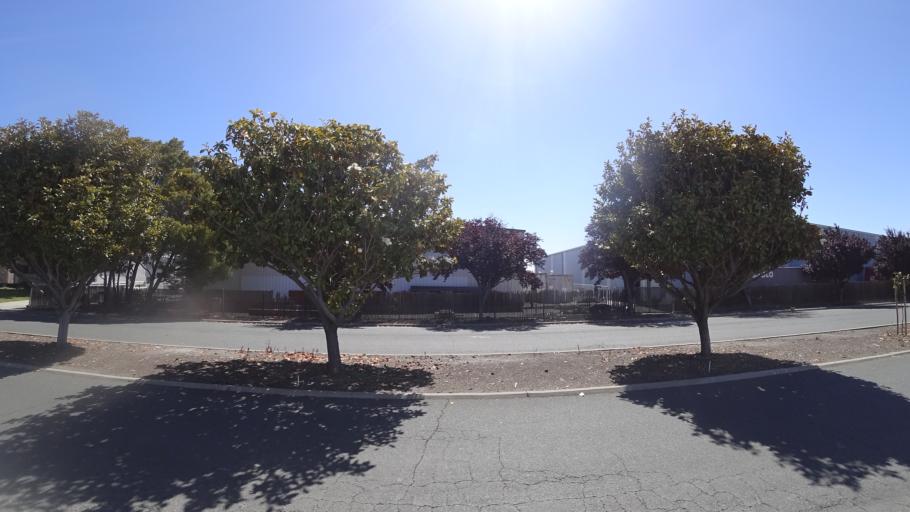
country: US
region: California
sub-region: Alameda County
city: San Lorenzo
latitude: 37.6551
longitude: -122.1248
